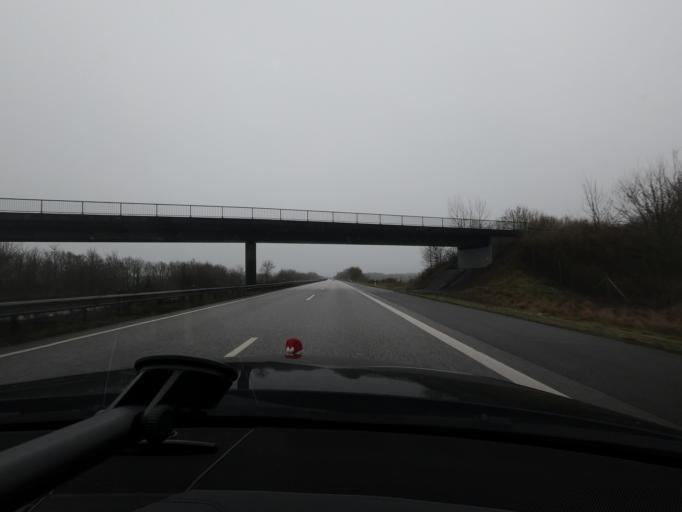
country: DE
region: Schleswig-Holstein
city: Bollingstedt
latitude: 54.6033
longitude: 9.4509
